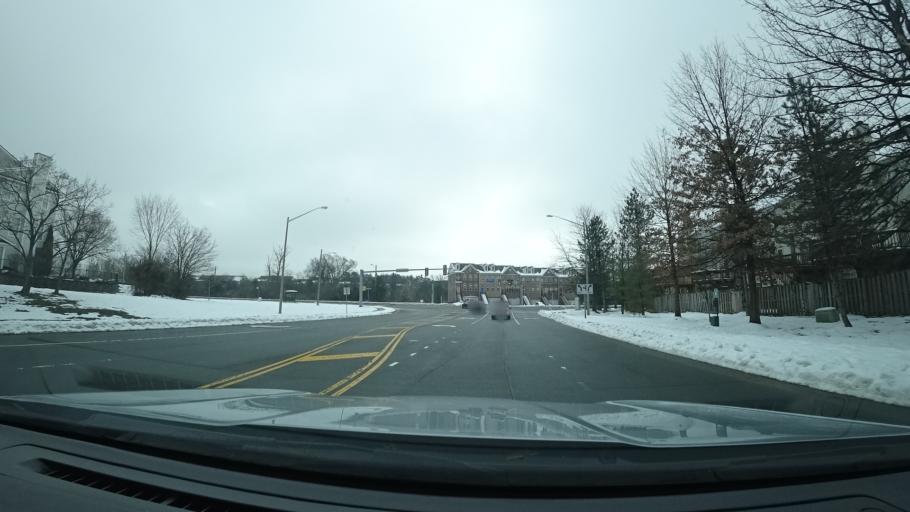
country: US
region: Virginia
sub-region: Fairfax County
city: Floris
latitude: 38.9454
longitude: -77.3994
